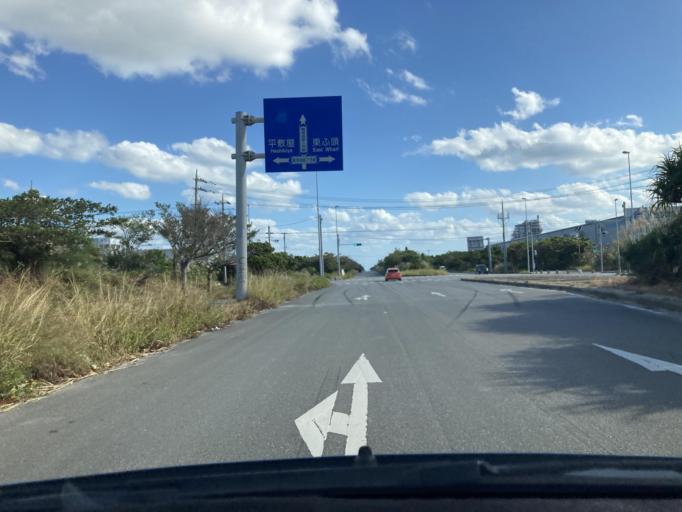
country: JP
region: Okinawa
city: Katsuren-haebaru
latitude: 26.3360
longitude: 127.8635
